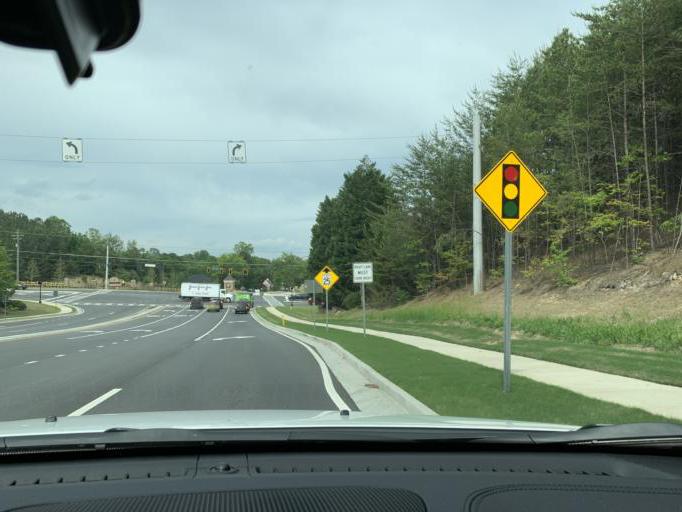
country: US
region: Georgia
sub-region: Gwinnett County
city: Sugar Hill
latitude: 34.1361
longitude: -84.1020
